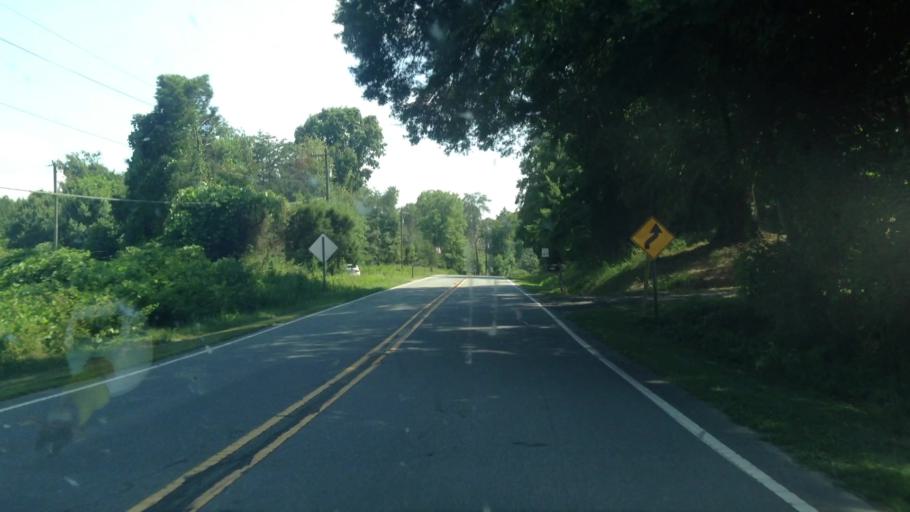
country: US
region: North Carolina
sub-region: Stokes County
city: Walnut Cove
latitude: 36.3239
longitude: -80.0496
